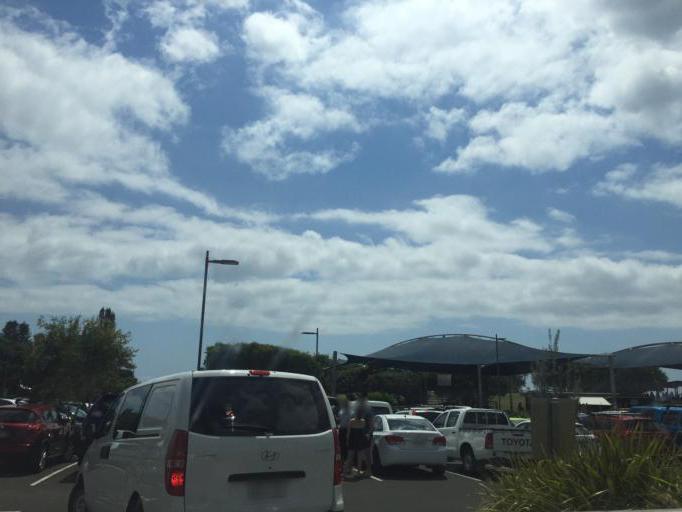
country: AU
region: Queensland
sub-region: Sunshine Coast
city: Coolum Beach
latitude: -26.5300
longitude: 153.0914
